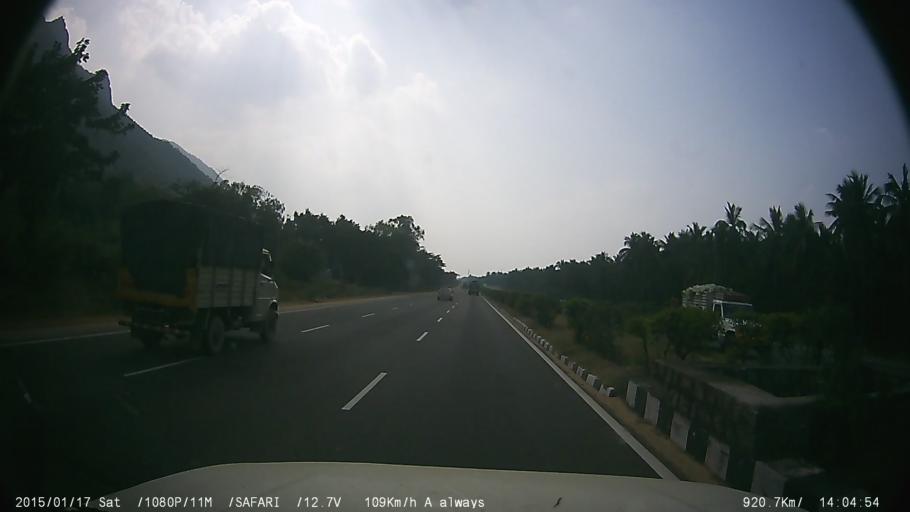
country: IN
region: Tamil Nadu
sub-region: Vellore
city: Odugattur
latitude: 12.8518
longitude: 78.8139
